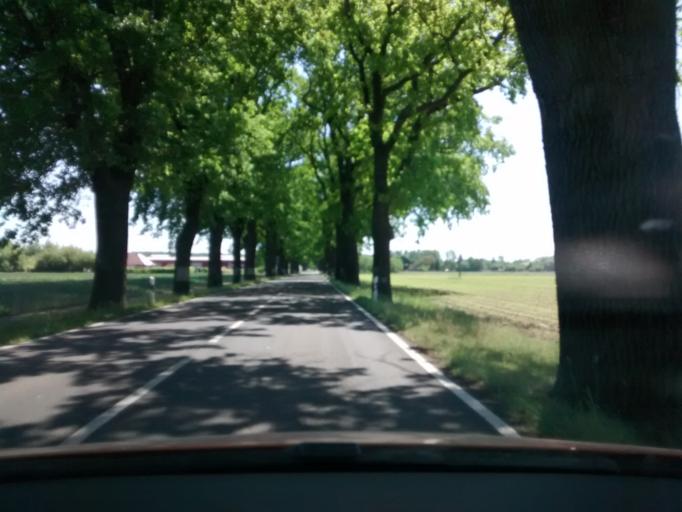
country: DE
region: Brandenburg
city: Storkow
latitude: 52.2667
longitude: 13.9295
